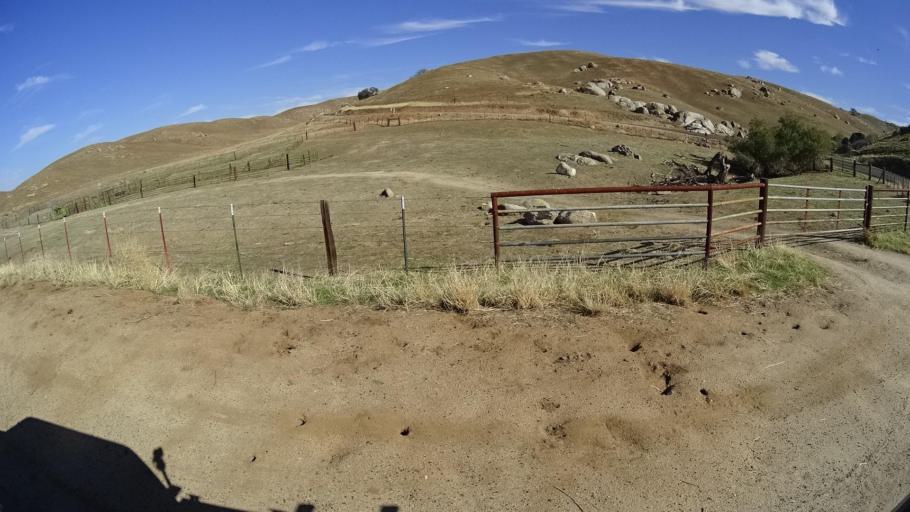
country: US
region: California
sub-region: Tulare County
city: Richgrove
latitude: 35.6830
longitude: -118.8893
